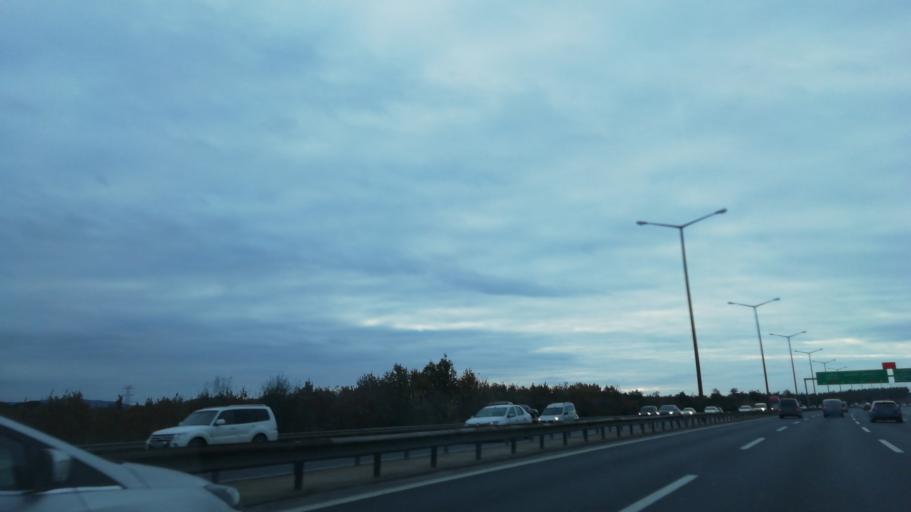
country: TR
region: Istanbul
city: Umraniye
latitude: 41.0624
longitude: 29.1143
